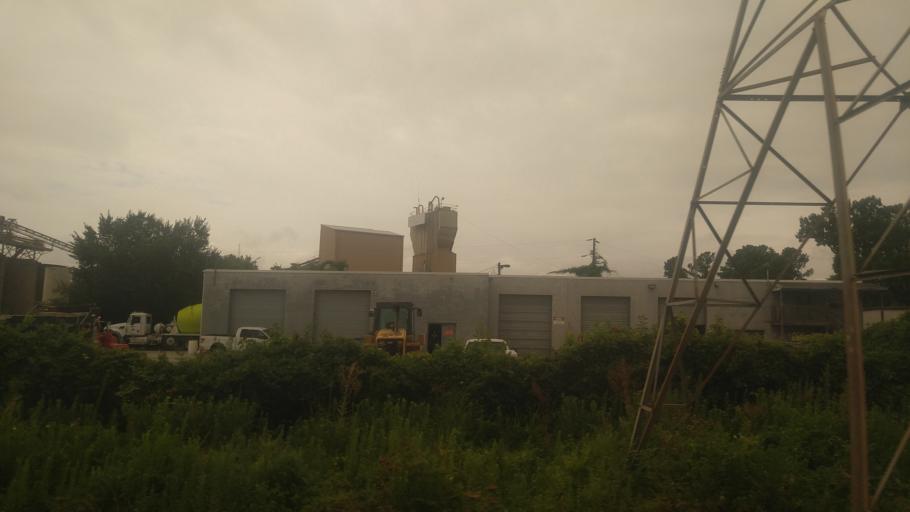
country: US
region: Virginia
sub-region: Henrico County
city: Dumbarton
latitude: 37.5908
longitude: -77.4823
